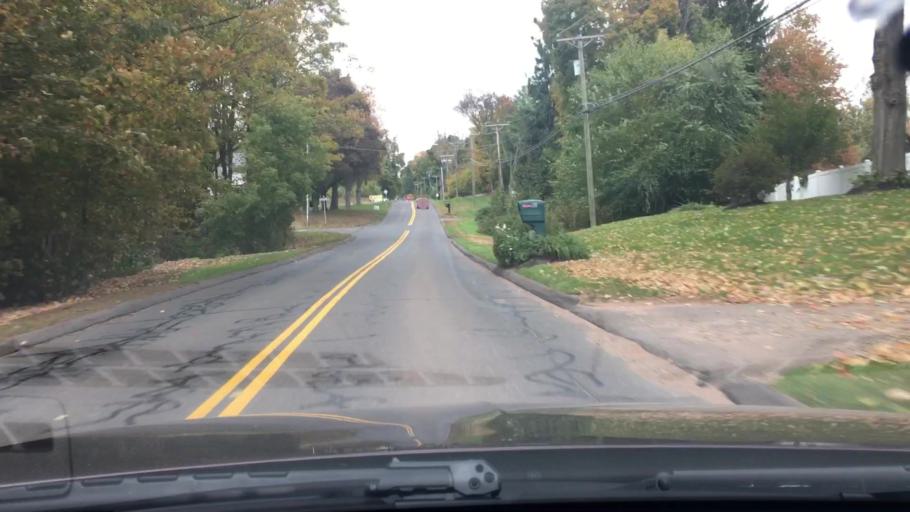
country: US
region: Connecticut
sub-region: Hartford County
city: Manchester
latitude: 41.8198
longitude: -72.5336
